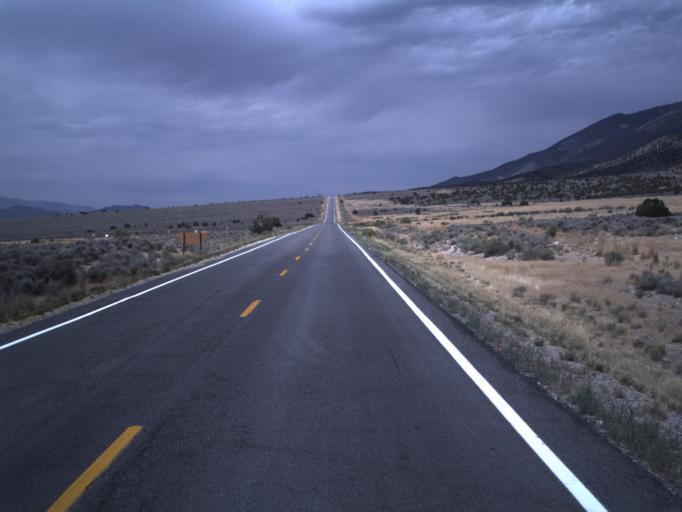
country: US
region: Utah
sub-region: Tooele County
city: Tooele
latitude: 40.3029
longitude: -112.2776
